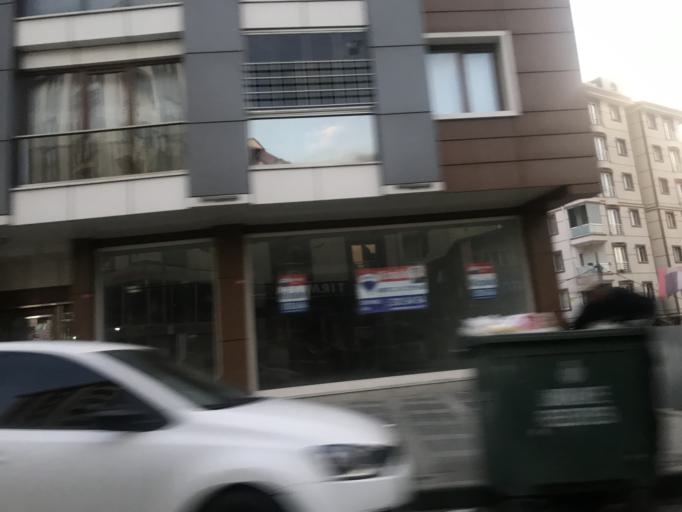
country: TR
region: Istanbul
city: Umraniye
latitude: 41.0355
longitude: 29.1020
